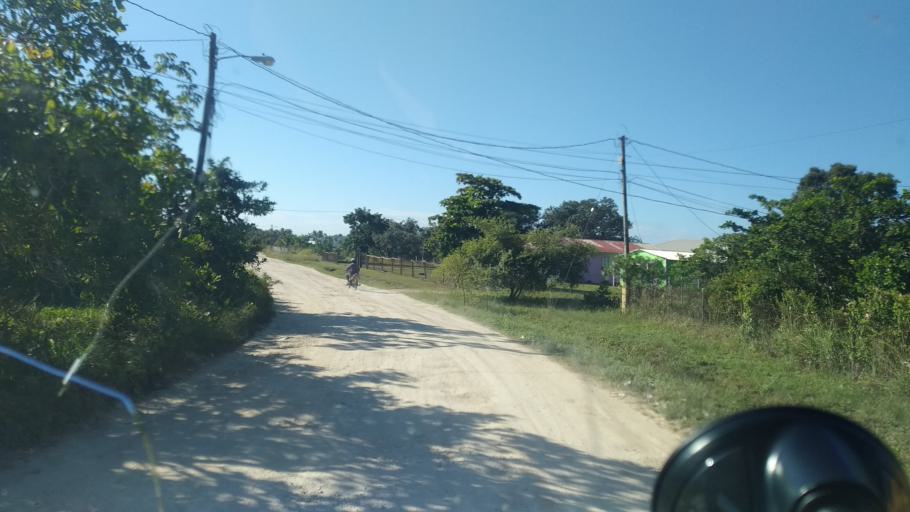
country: BZ
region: Belize
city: Belize City
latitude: 17.5537
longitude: -88.3261
